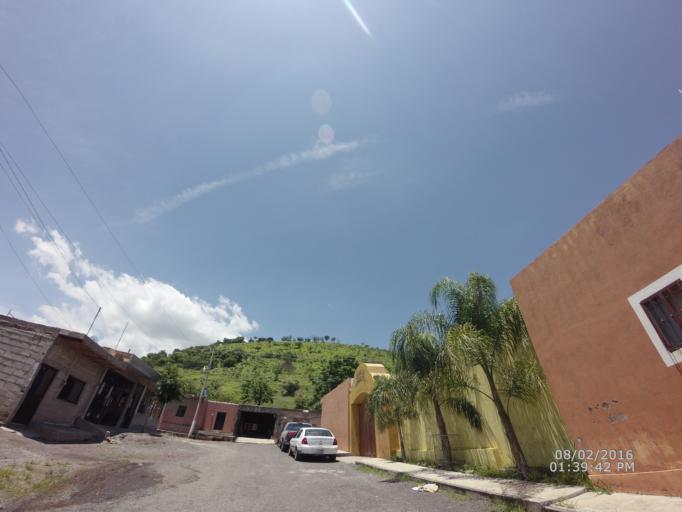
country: MX
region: Nayarit
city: Ixtlan del Rio
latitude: 21.0322
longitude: -104.3575
